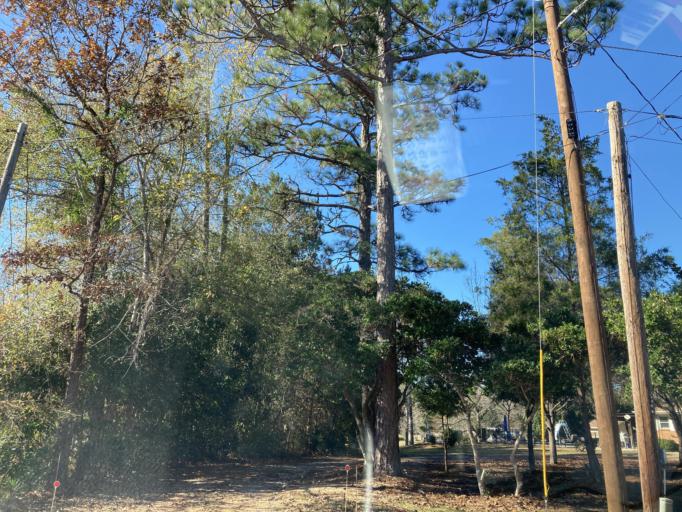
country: US
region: Mississippi
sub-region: Forrest County
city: Petal
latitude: 31.3576
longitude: -89.1646
